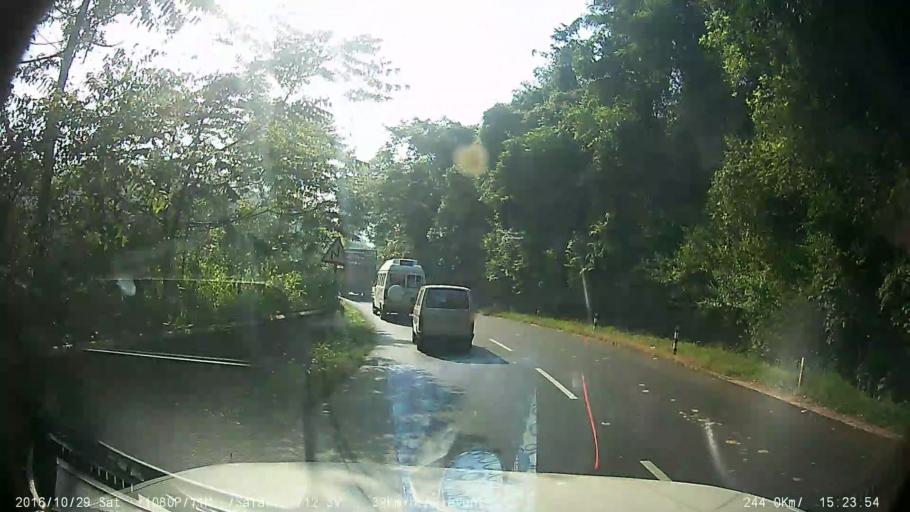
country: IN
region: Karnataka
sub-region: Kodagu
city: Madikeri
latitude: 12.4289
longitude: 75.7788
